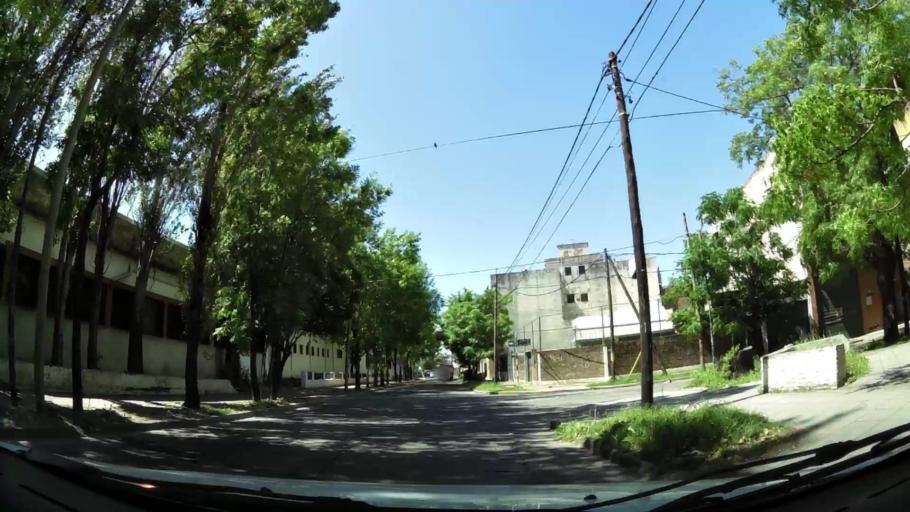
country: AR
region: Buenos Aires
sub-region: Partido de General San Martin
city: General San Martin
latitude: -34.5678
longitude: -58.5519
